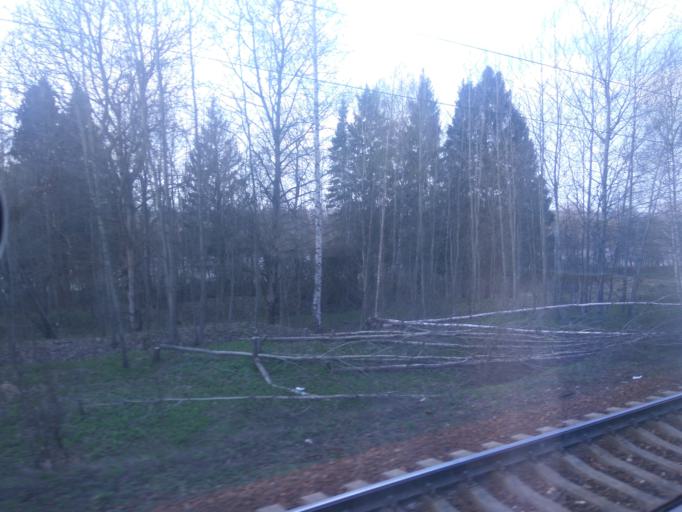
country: RU
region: Moskovskaya
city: Dedenevo
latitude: 56.2694
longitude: 37.5085
